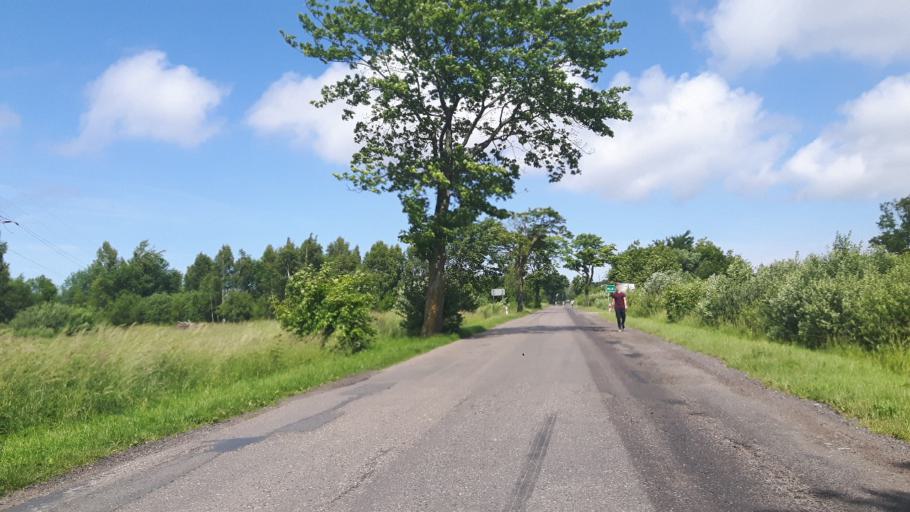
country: PL
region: Pomeranian Voivodeship
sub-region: Powiat slupski
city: Ustka
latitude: 54.5598
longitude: 16.8438
